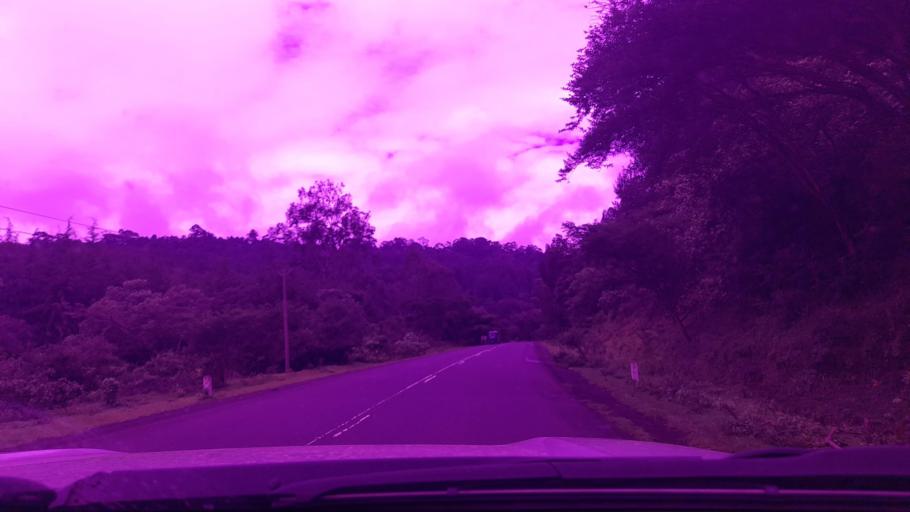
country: ET
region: Oromiya
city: Jima
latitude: 7.5558
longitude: 36.5900
